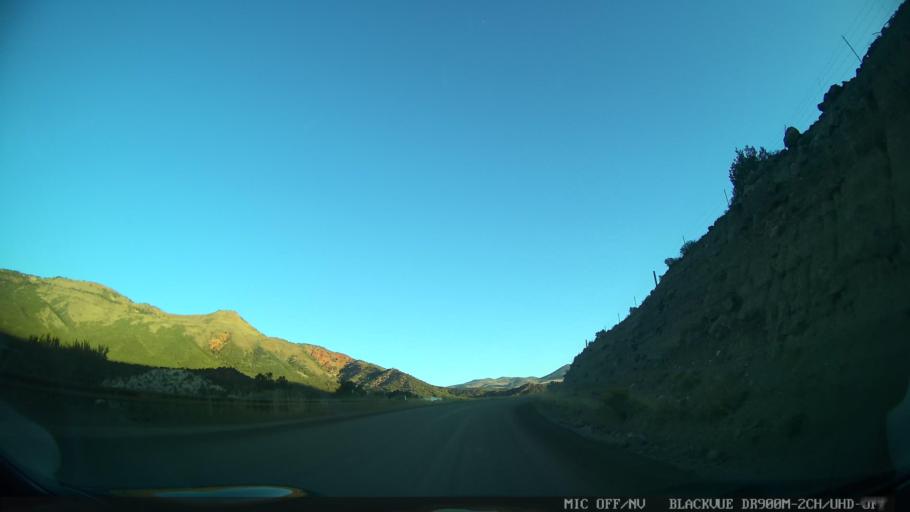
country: US
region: Colorado
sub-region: Eagle County
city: Edwards
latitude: 39.8975
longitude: -106.6068
